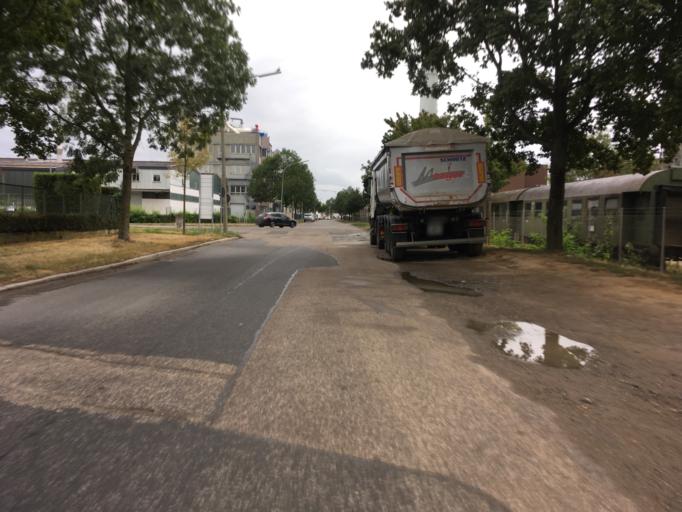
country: DE
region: Baden-Wuerttemberg
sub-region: Regierungsbezirk Stuttgart
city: Neckarsulm
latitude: 49.1758
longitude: 9.2097
